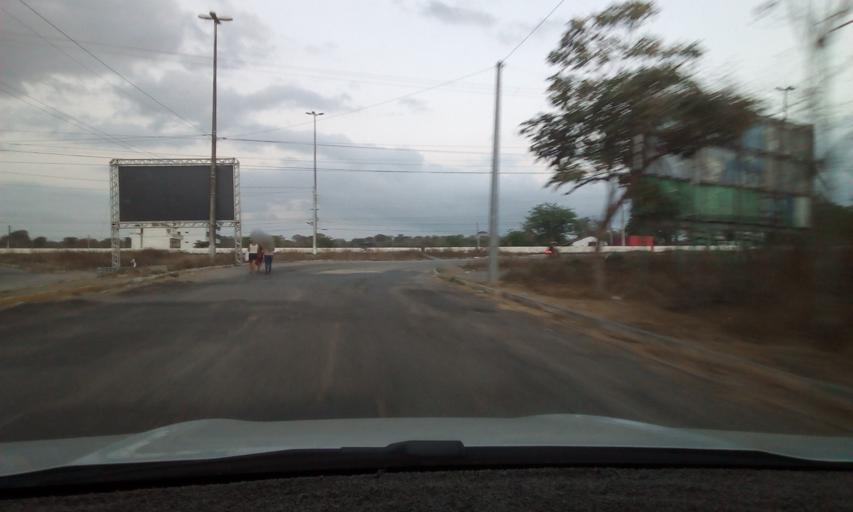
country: BR
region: Pernambuco
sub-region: Caruaru
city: Caruaru
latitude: -8.2420
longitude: -35.9761
